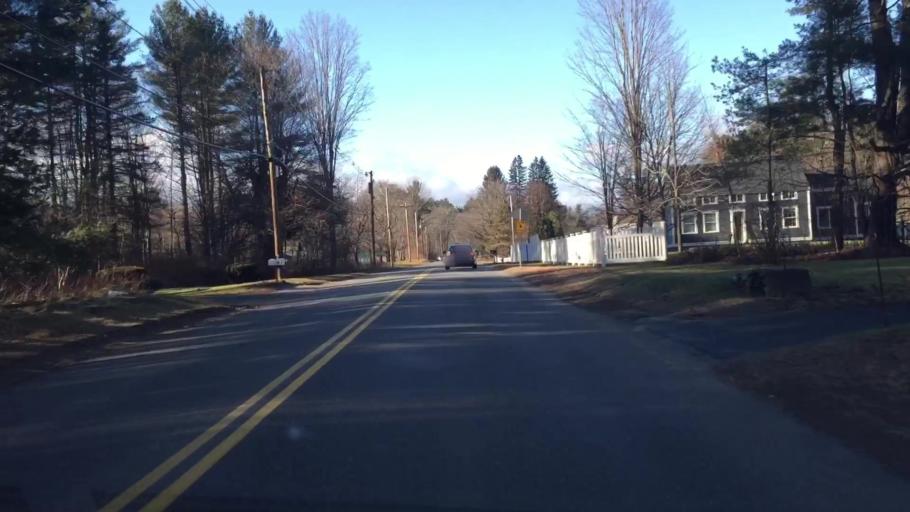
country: US
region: Massachusetts
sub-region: Worcester County
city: Sterling
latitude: 42.4342
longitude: -71.8144
